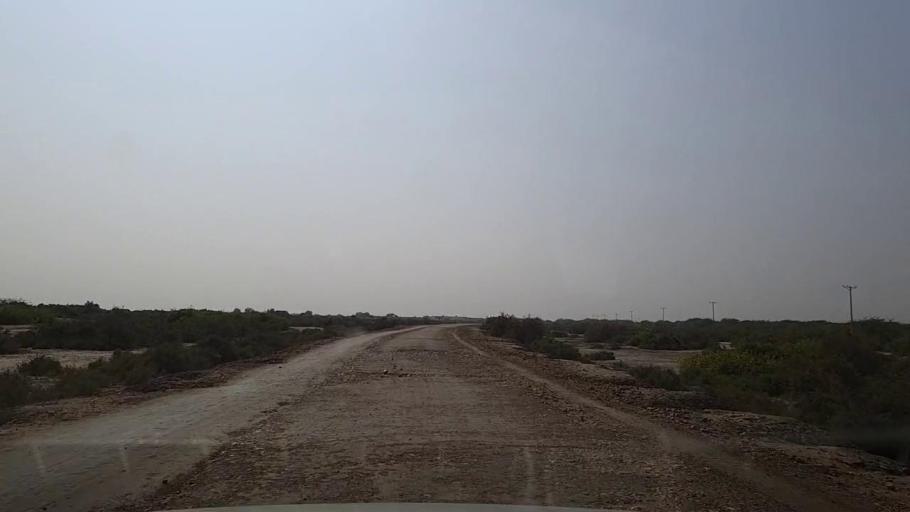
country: PK
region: Sindh
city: Mirpur Sakro
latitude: 24.5330
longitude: 67.5933
